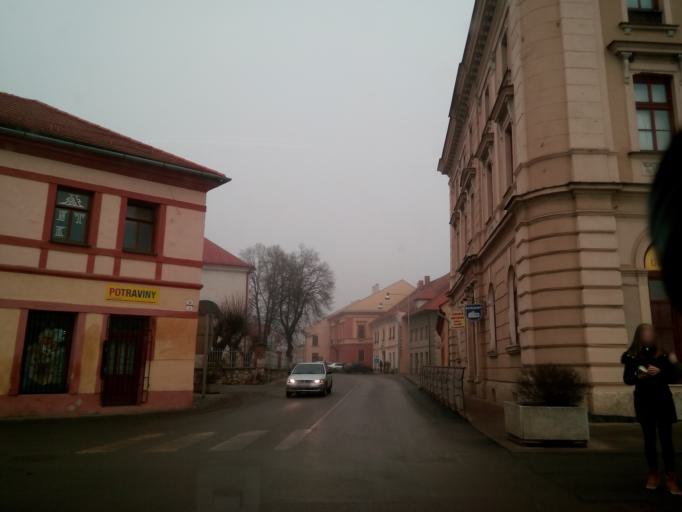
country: SK
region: Presovsky
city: Spisske Podhradie
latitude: 49.0004
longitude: 20.7520
